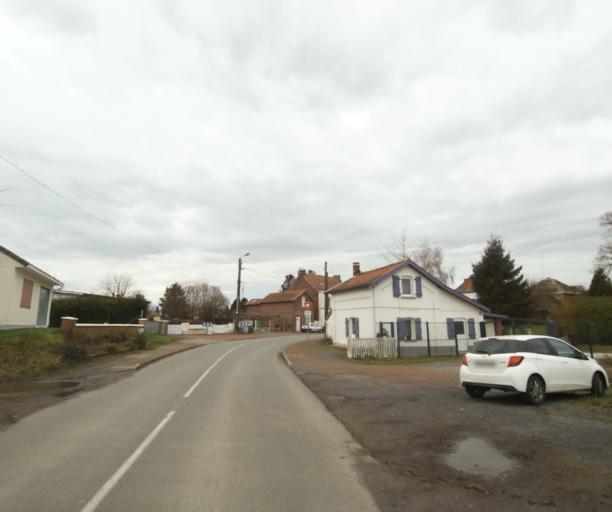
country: FR
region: Nord-Pas-de-Calais
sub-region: Departement du Nord
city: Curgies
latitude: 50.3283
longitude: 3.6110
